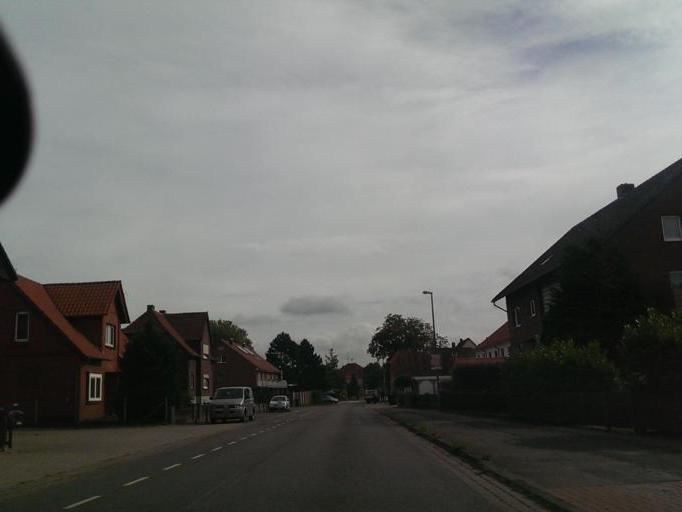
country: DE
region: Lower Saxony
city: Garbsen-Mitte
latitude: 52.4628
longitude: 9.5990
